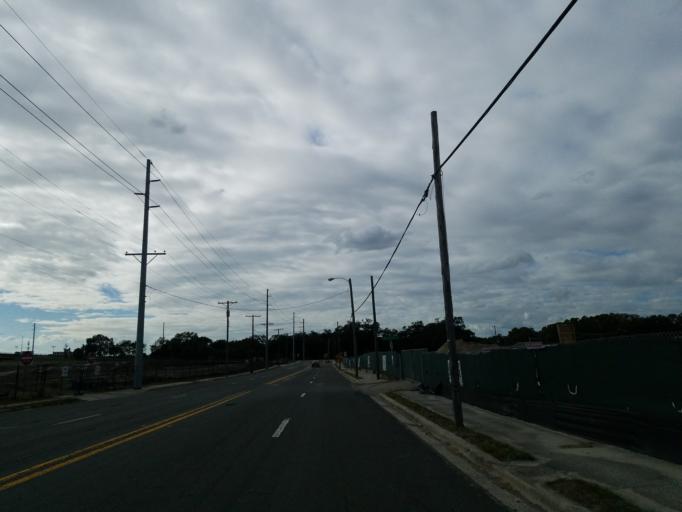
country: US
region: Florida
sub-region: Hillsborough County
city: Tampa
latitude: 27.9623
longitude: -82.4652
